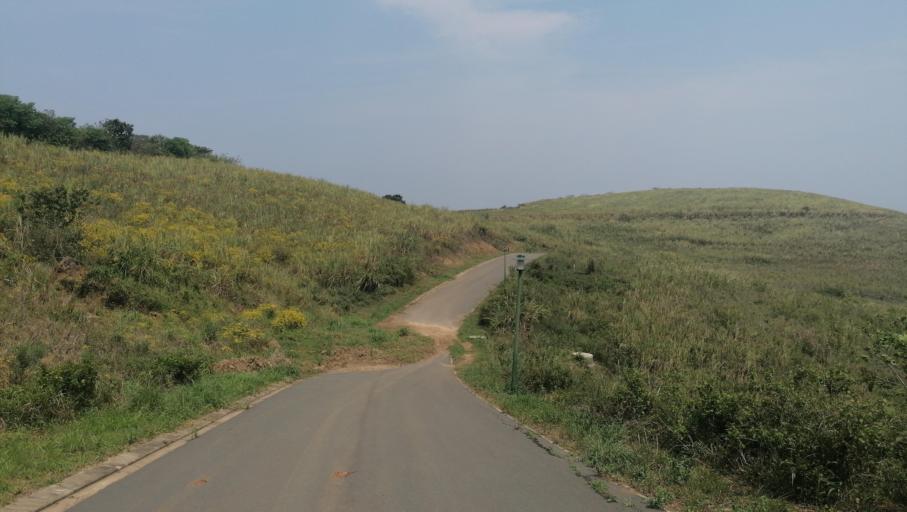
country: ZA
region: KwaZulu-Natal
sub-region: iLembe District Municipality
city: Stanger
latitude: -29.4300
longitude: 31.2670
